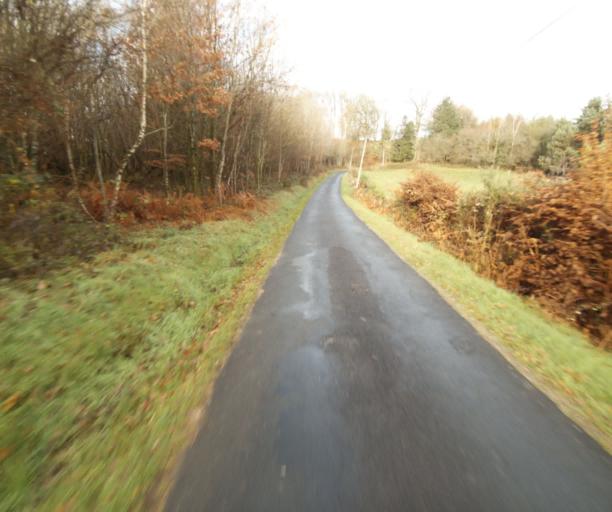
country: FR
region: Limousin
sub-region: Departement de la Correze
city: Saint-Mexant
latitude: 45.2583
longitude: 1.6401
